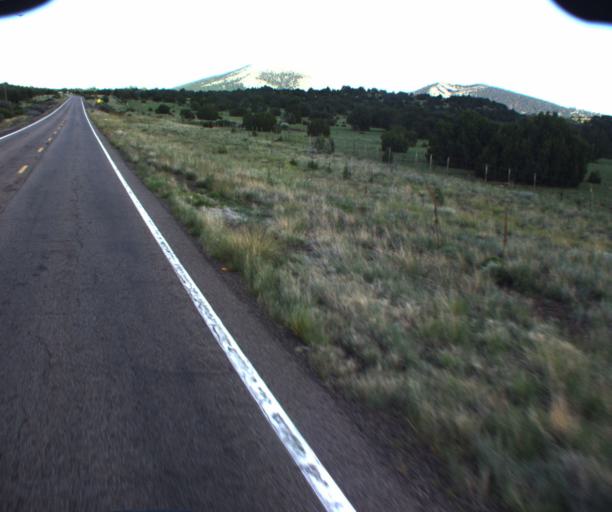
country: US
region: Arizona
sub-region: Apache County
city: Saint Johns
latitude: 34.2681
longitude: -109.6232
